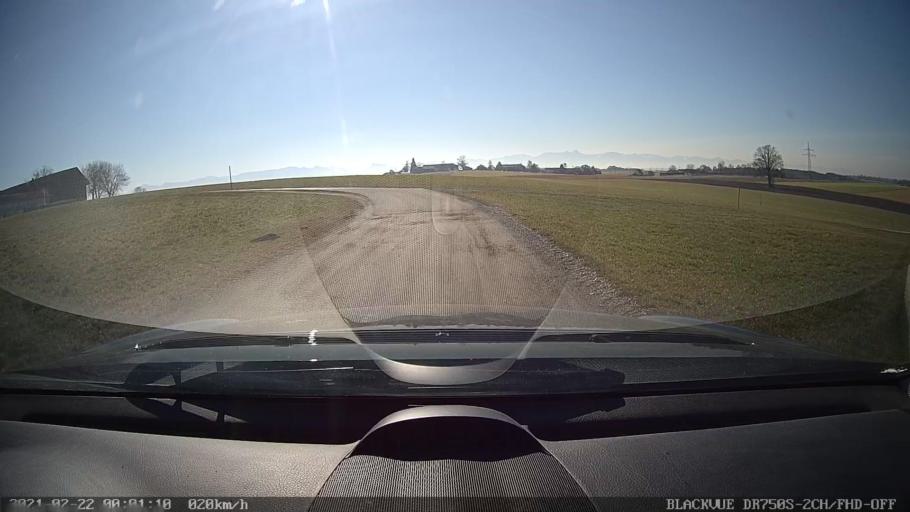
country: DE
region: Bavaria
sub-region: Upper Bavaria
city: Griesstatt
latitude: 47.9851
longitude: 12.1870
